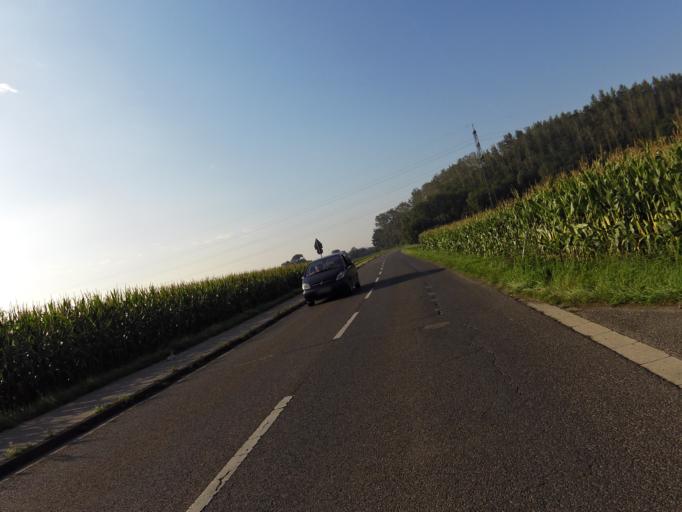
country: DE
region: North Rhine-Westphalia
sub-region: Regierungsbezirk Koln
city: Ubach-Palenberg
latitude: 50.9292
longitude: 6.1231
